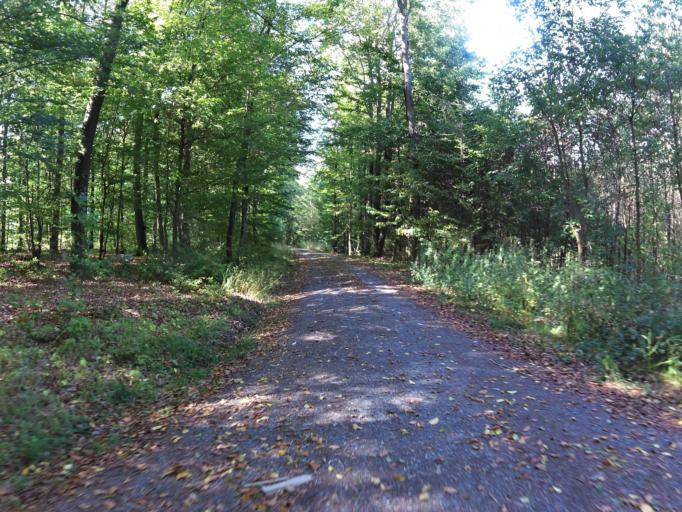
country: DE
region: Bavaria
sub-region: Regierungsbezirk Unterfranken
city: Eisingen
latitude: 49.7721
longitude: 9.8306
